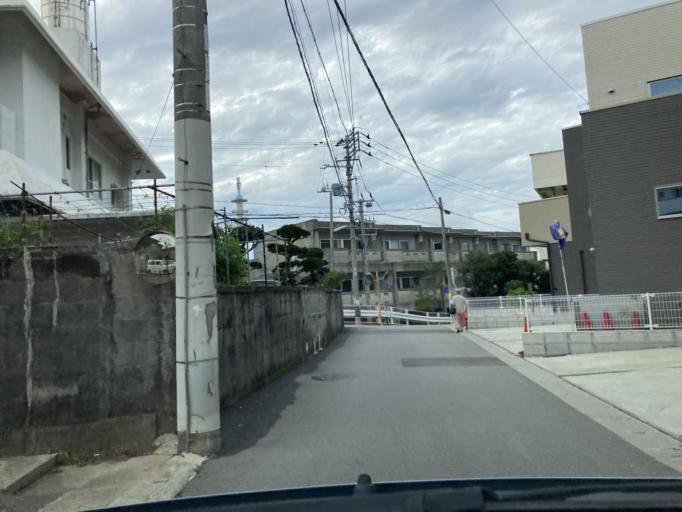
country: JP
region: Okinawa
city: Naha-shi
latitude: 26.2195
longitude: 127.7299
